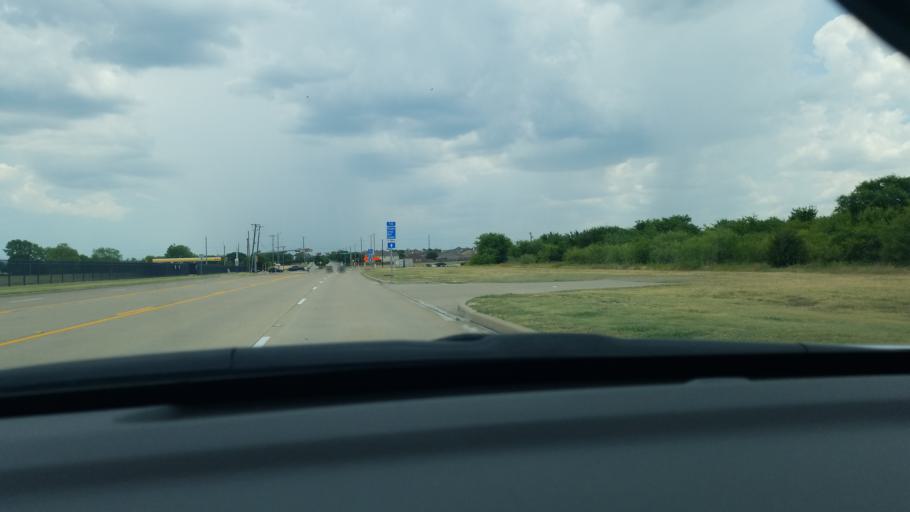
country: US
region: Texas
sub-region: Dallas County
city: Grand Prairie
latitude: 32.6914
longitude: -97.0467
